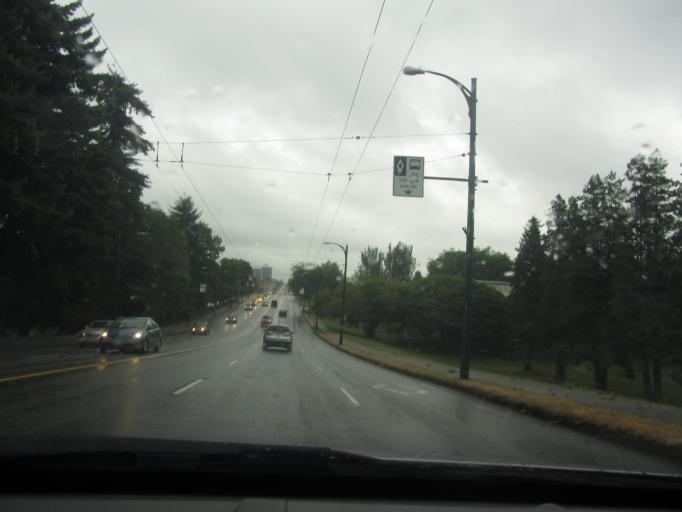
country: CA
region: British Columbia
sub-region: Fraser Valley Regional District
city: North Vancouver
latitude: 49.2811
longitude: -123.0411
